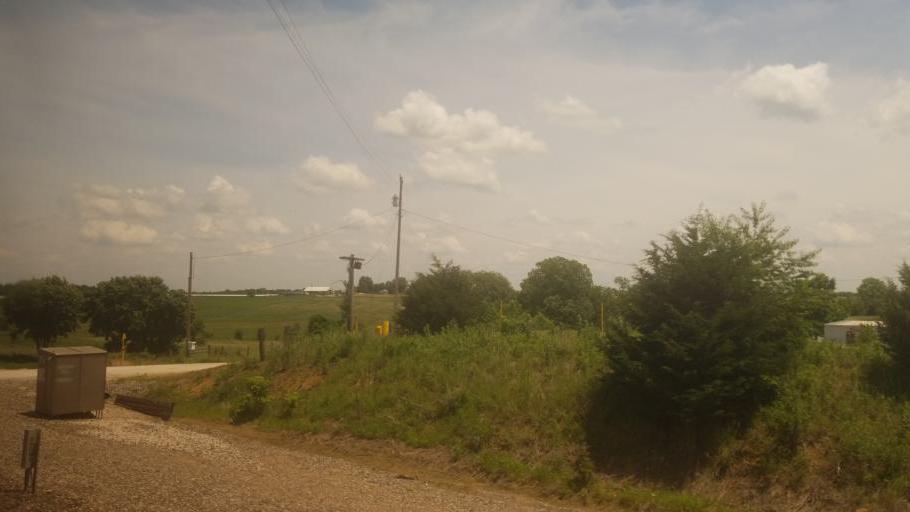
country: US
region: Missouri
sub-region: Macon County
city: La Plata
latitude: 40.0369
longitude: -92.4779
